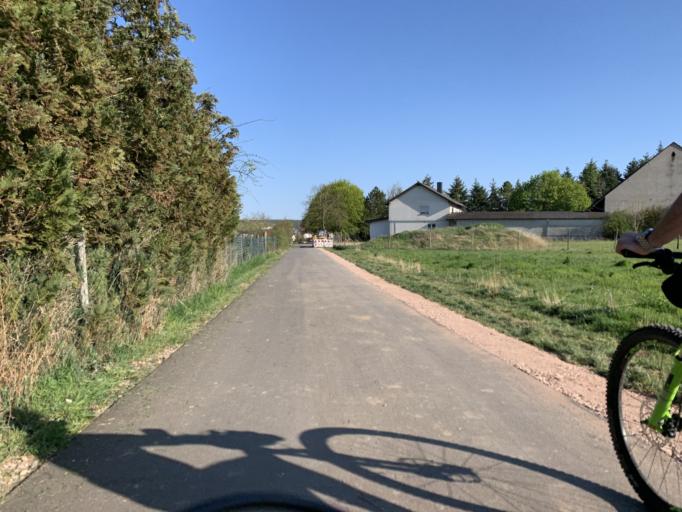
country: DE
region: Rheinland-Pfalz
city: Windesheim
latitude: 49.8992
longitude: 7.8314
